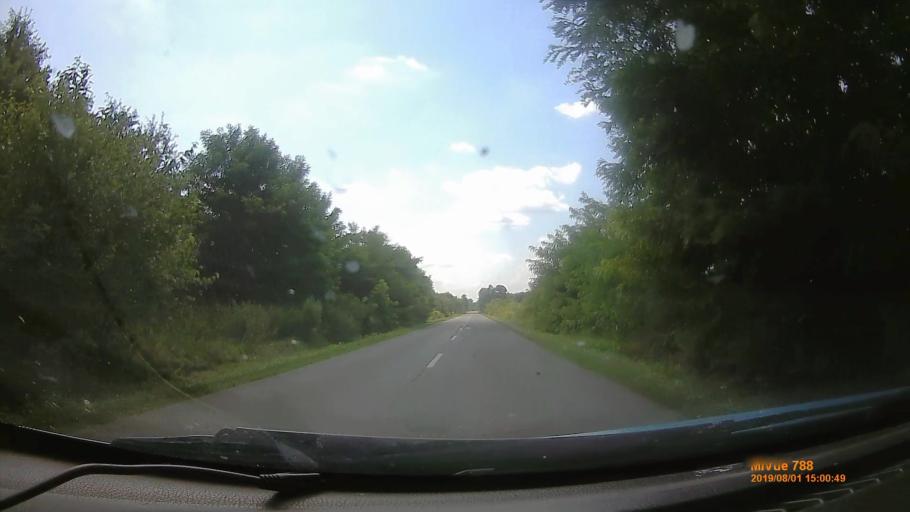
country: HU
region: Baranya
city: Sellye
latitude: 45.8816
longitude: 17.8905
